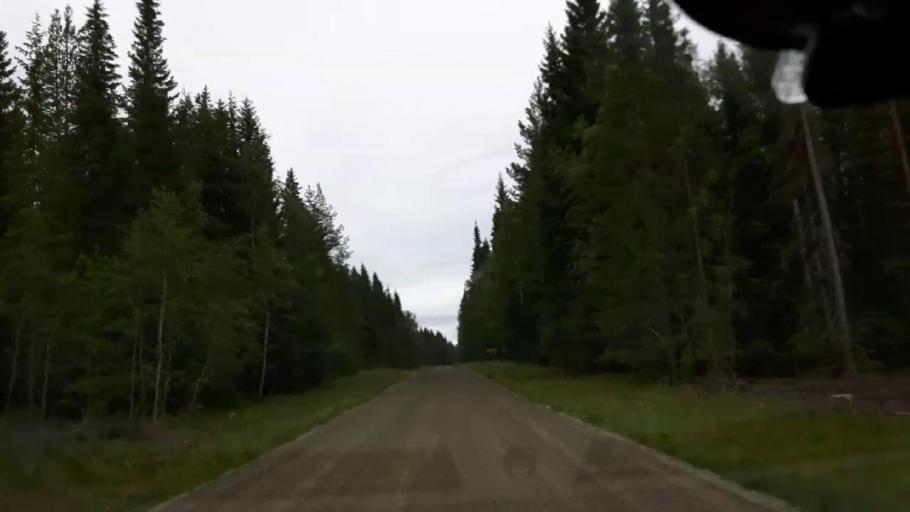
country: SE
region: Jaemtland
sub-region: Braecke Kommun
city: Braecke
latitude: 62.9794
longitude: 15.4028
